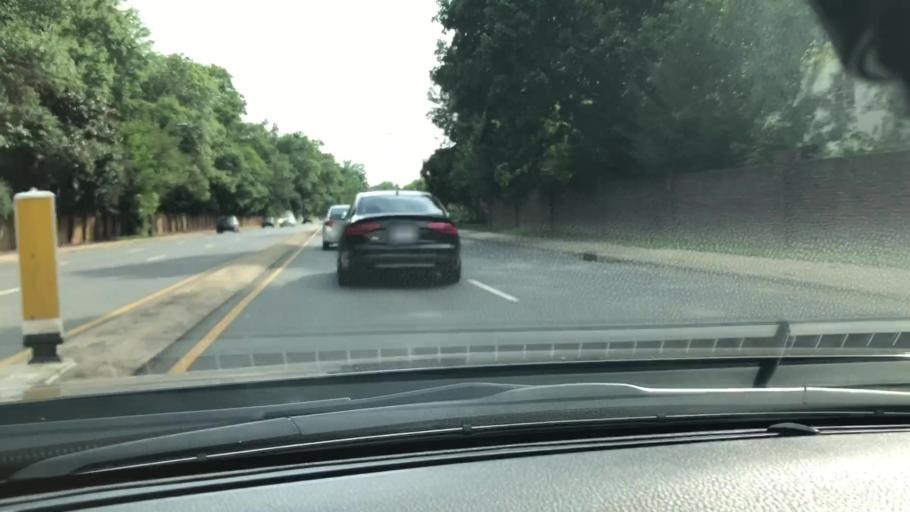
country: US
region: North Carolina
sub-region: Mecklenburg County
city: Charlotte
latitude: 35.1585
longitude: -80.8216
